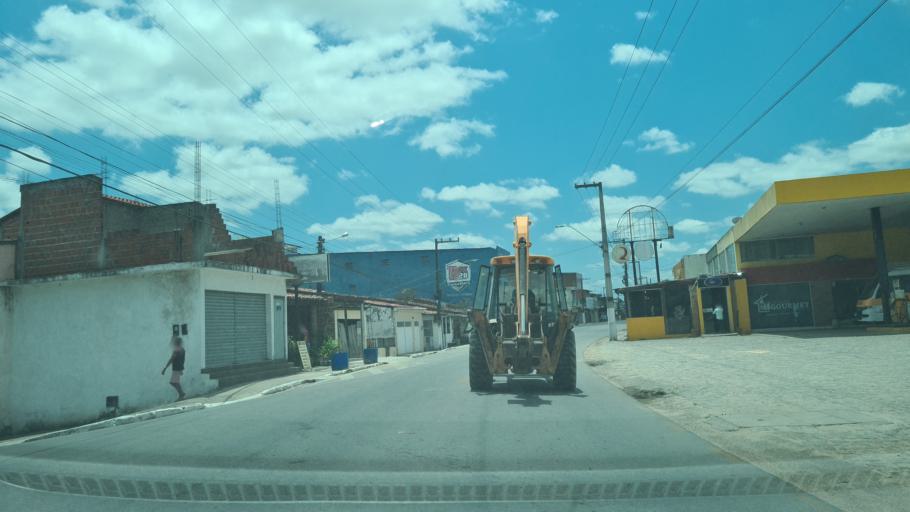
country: BR
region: Alagoas
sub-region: Uniao Dos Palmares
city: Uniao dos Palmares
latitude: -9.1642
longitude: -36.0274
